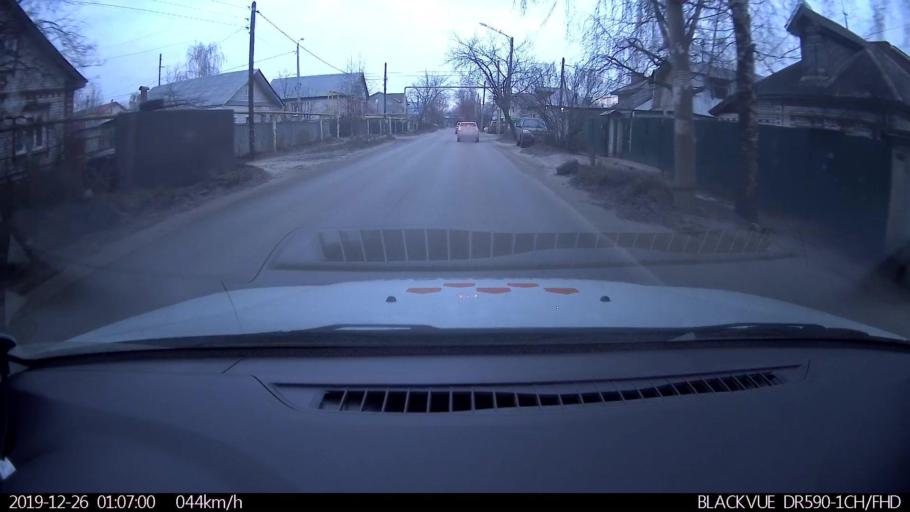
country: RU
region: Nizjnij Novgorod
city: Nizhniy Novgorod
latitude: 56.2794
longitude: 43.9058
